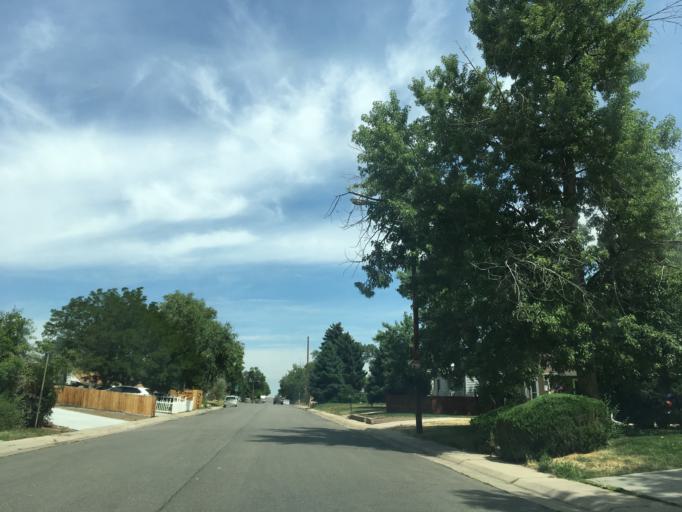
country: US
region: Colorado
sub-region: Jefferson County
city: Lakewood
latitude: 39.6938
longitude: -105.0402
